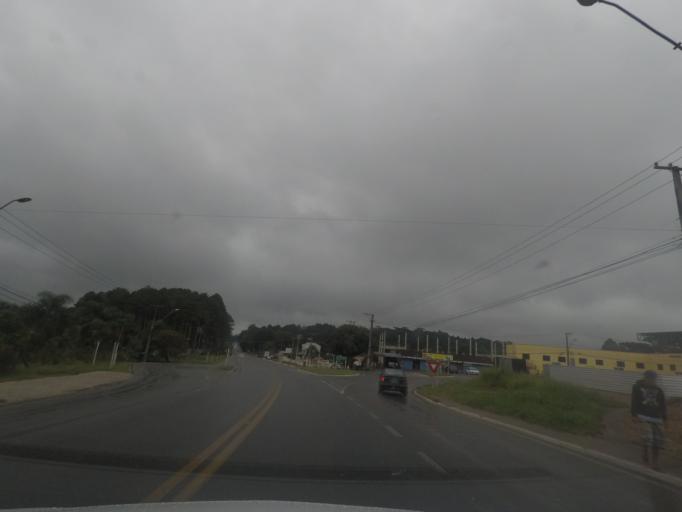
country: BR
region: Parana
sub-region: Colombo
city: Colombo
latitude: -25.3405
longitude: -49.1574
